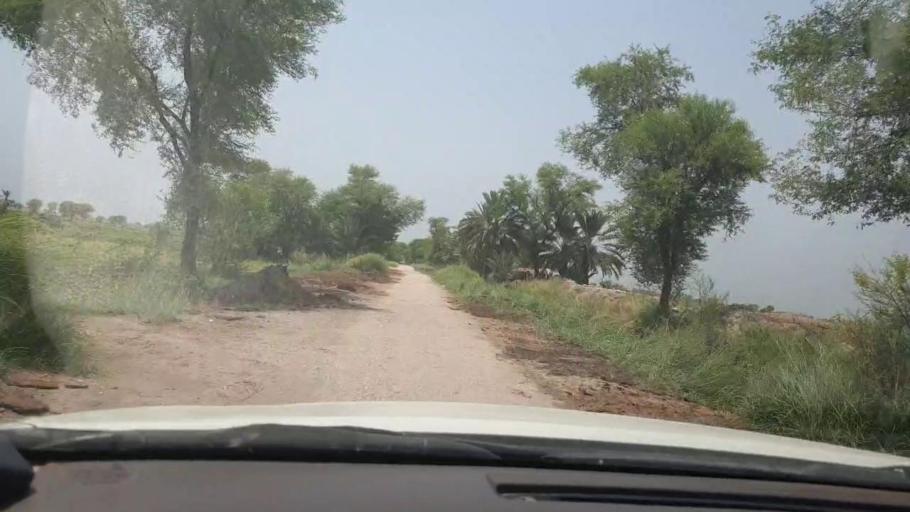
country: PK
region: Sindh
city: Garhi Yasin
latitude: 27.9108
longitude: 68.5571
